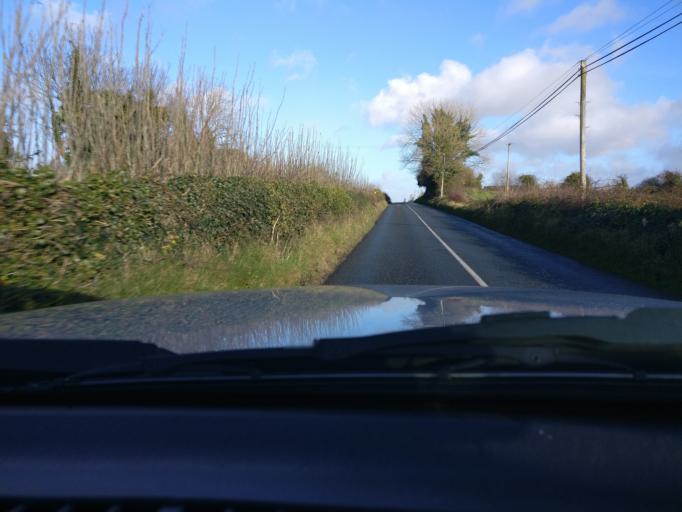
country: IE
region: Leinster
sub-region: An Iarmhi
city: Kilbeggan
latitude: 53.4531
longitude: -7.5253
